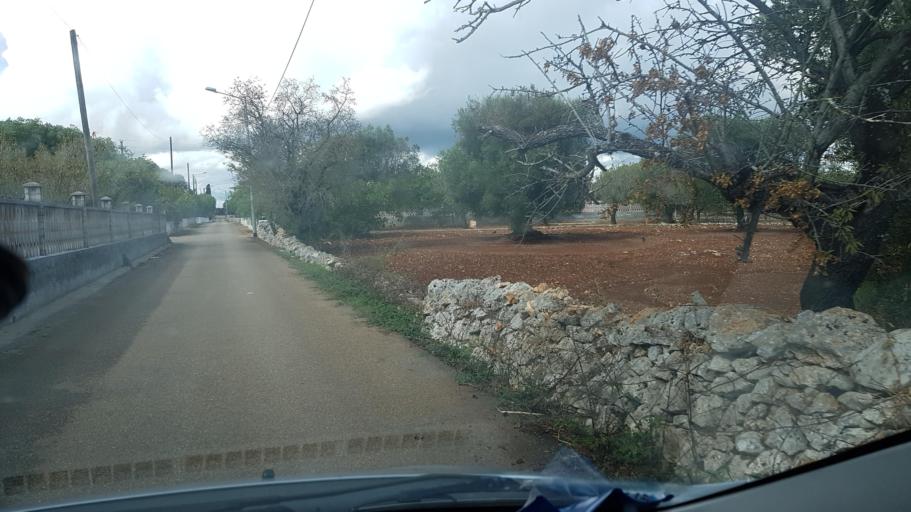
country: IT
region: Apulia
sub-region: Provincia di Brindisi
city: San Vito dei Normanni
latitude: 40.6538
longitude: 17.7336
